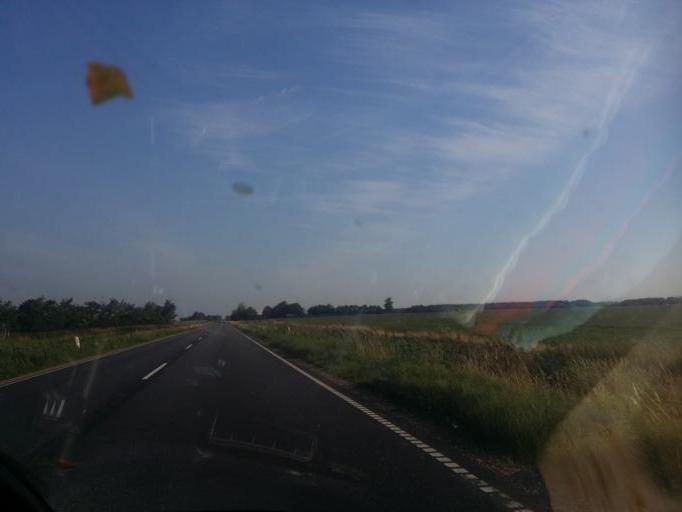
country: DK
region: South Denmark
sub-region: Esbjerg Kommune
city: Ribe
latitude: 55.2458
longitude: 8.7235
